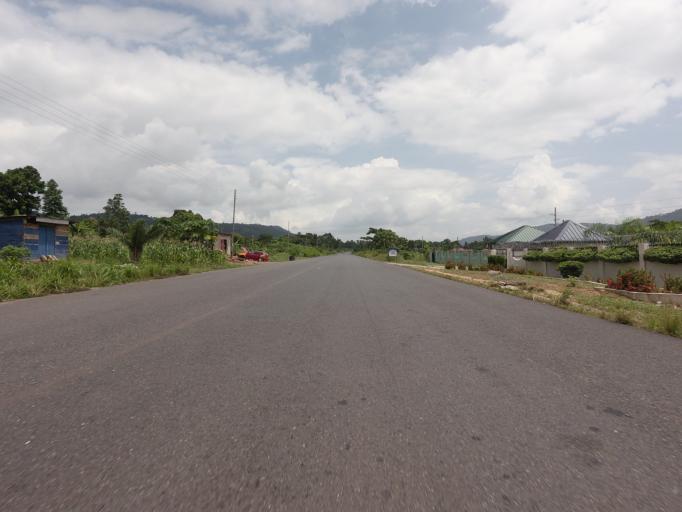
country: GH
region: Volta
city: Ho
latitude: 6.5471
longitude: 0.2524
